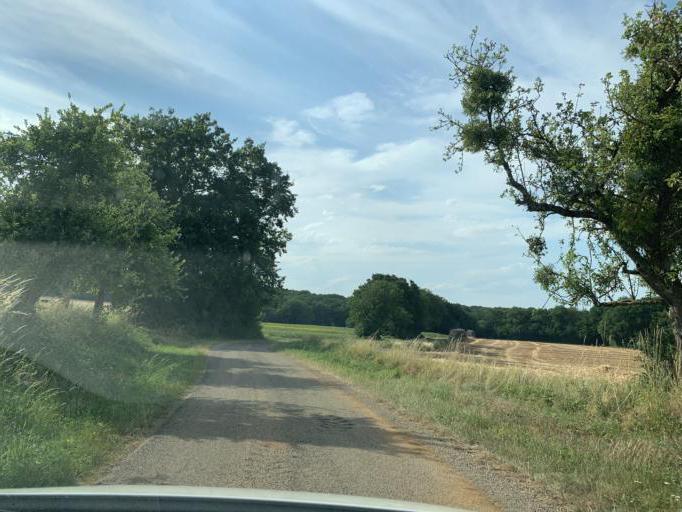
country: FR
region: Bourgogne
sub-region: Departement de l'Yonne
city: Fontenailles
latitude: 47.5037
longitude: 3.4294
